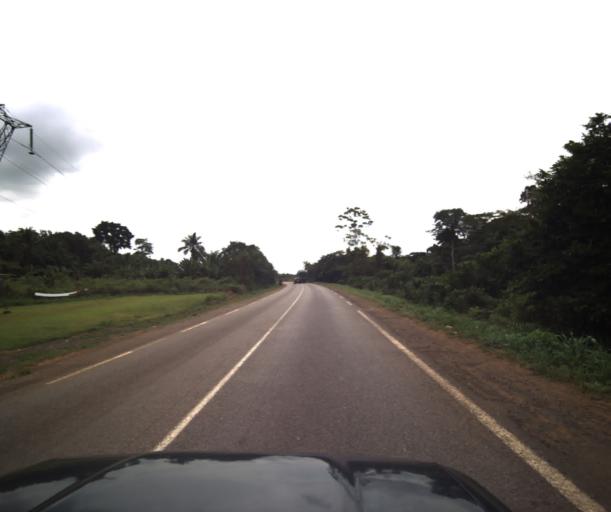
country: CM
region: Littoral
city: Edea
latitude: 3.8332
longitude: 10.4081
